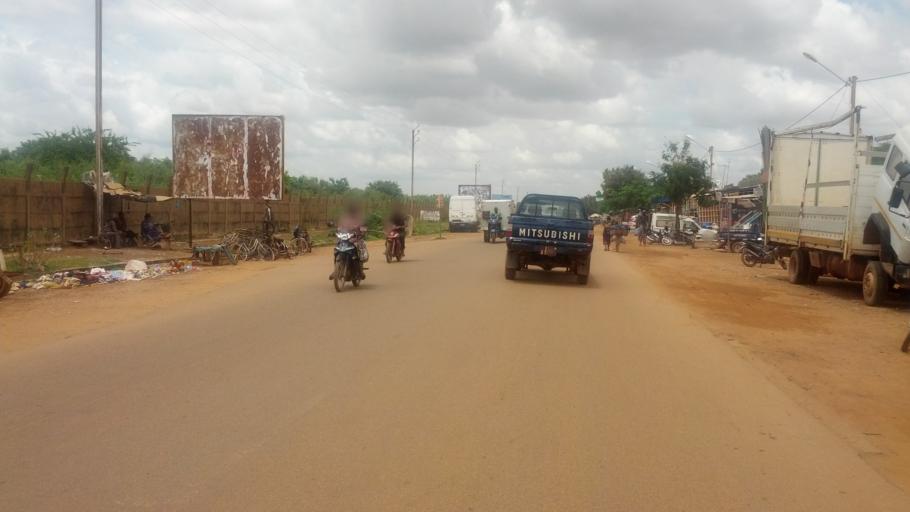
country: BF
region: Centre
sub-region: Kadiogo Province
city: Ouagadougou
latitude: 12.3459
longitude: -1.5039
